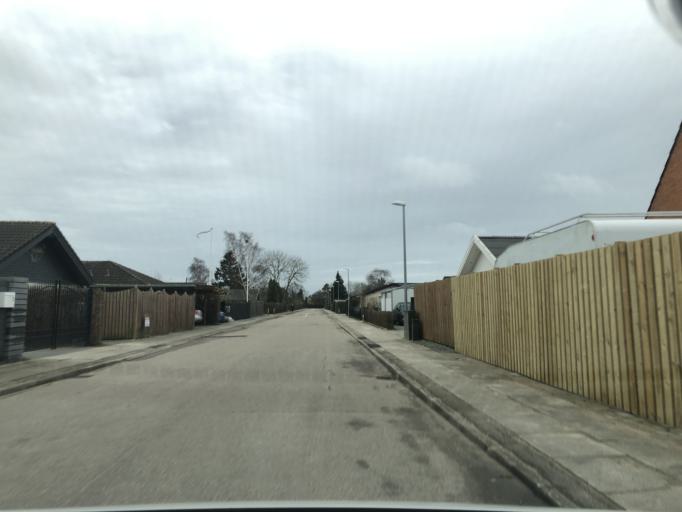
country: DK
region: Capital Region
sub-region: Tarnby Kommune
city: Tarnby
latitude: 55.5950
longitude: 12.5841
